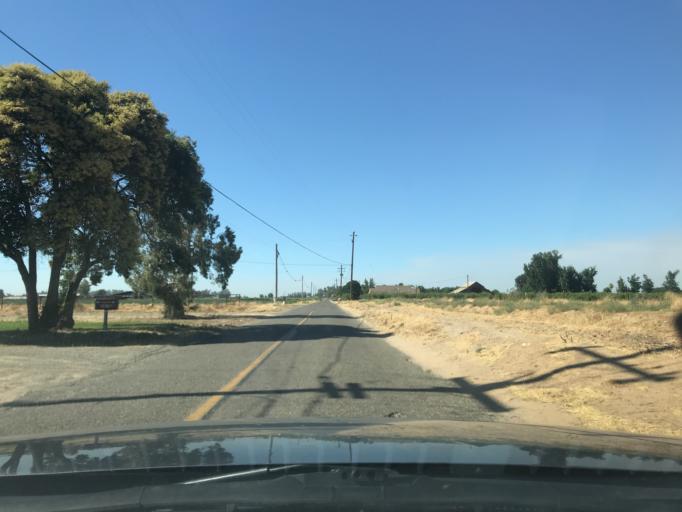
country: US
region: California
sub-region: Merced County
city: Atwater
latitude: 37.3266
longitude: -120.5500
